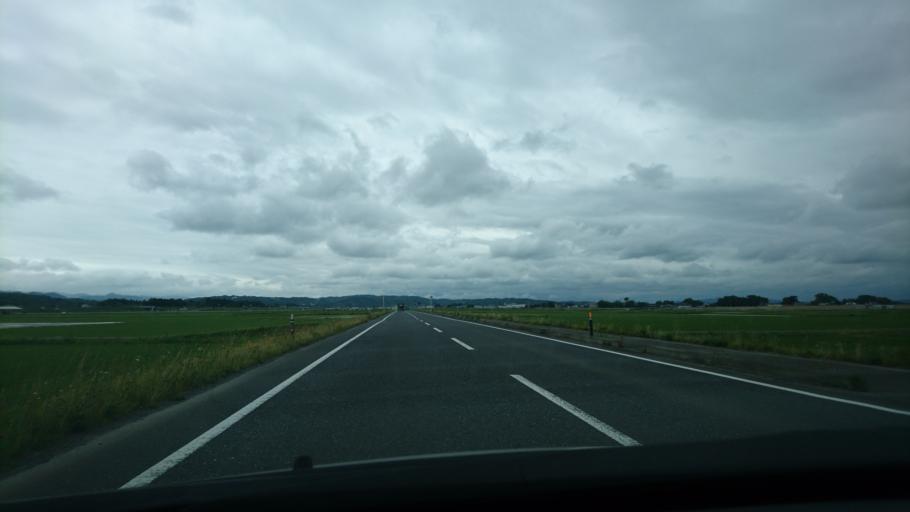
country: JP
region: Miyagi
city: Wakuya
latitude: 38.6848
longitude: 141.2610
